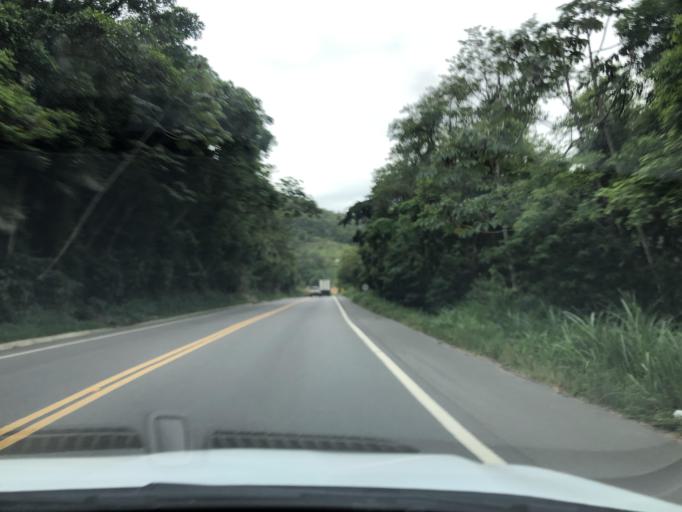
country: BR
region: Santa Catarina
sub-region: Ibirama
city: Ibirama
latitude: -27.0802
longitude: -49.5188
